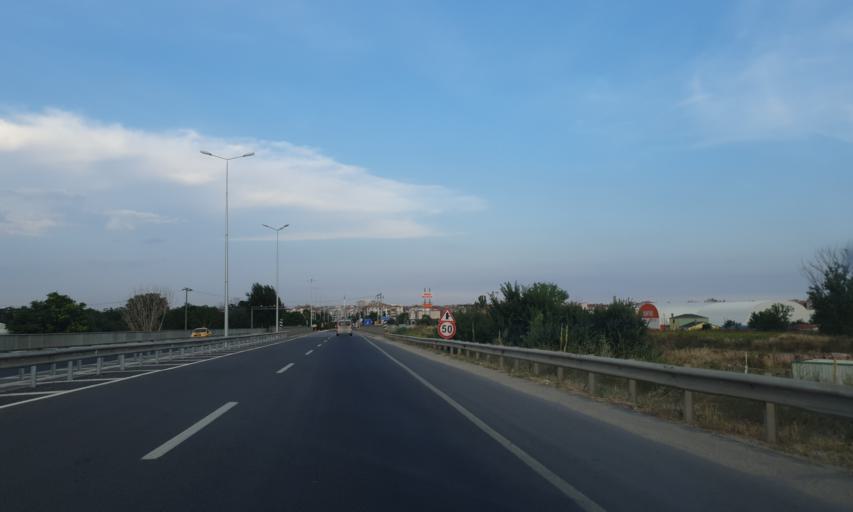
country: TR
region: Kirklareli
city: Luleburgaz
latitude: 41.4048
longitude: 27.3404
